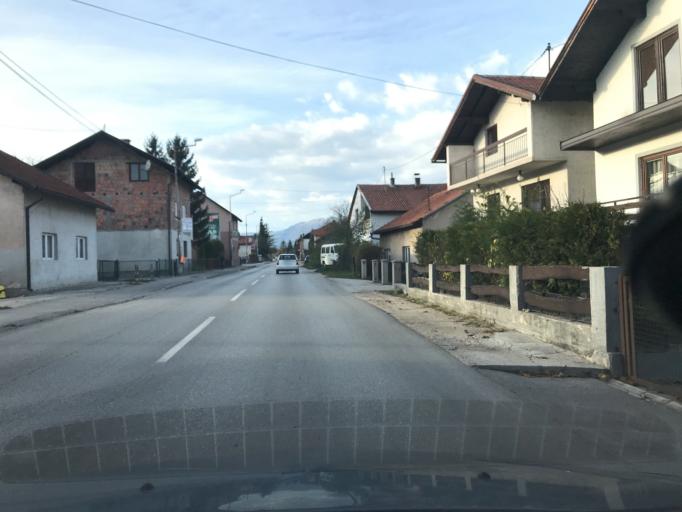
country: BA
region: Federation of Bosnia and Herzegovina
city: Vitez
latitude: 44.1587
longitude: 17.7862
